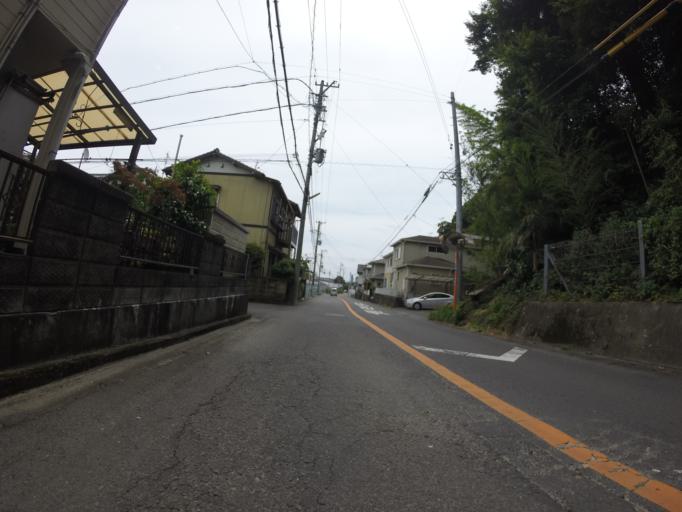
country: JP
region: Shizuoka
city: Shizuoka-shi
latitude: 35.0223
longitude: 138.4176
